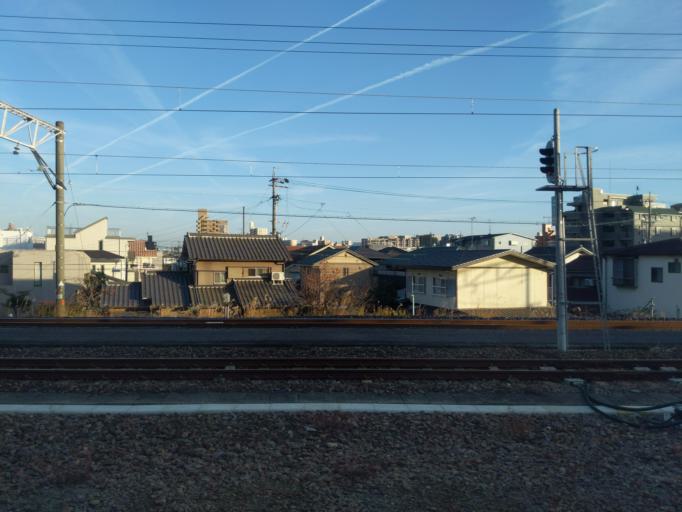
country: JP
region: Aichi
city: Kasugai
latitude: 35.2049
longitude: 136.9495
